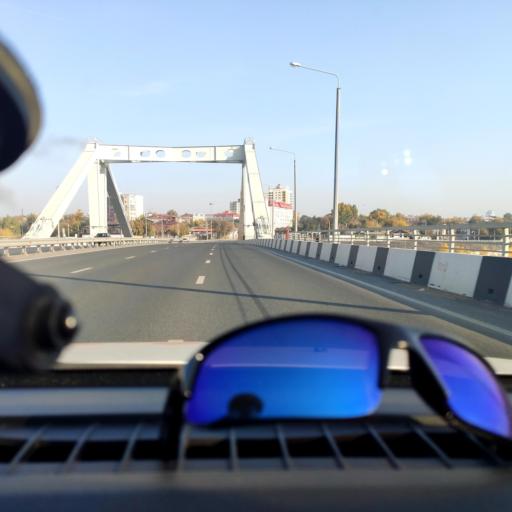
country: RU
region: Samara
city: Rozhdestveno
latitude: 53.1761
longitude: 50.0858
